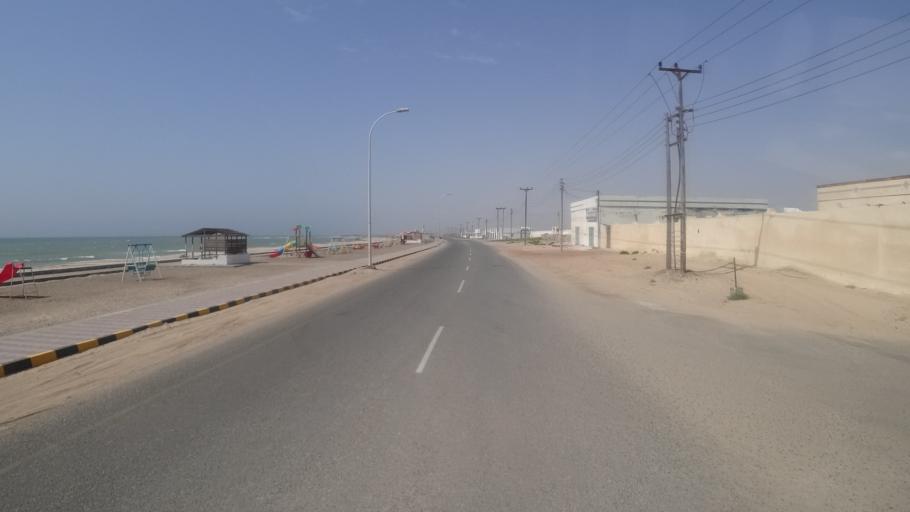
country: OM
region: Ash Sharqiyah
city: Sur
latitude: 22.1155
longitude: 59.7130
